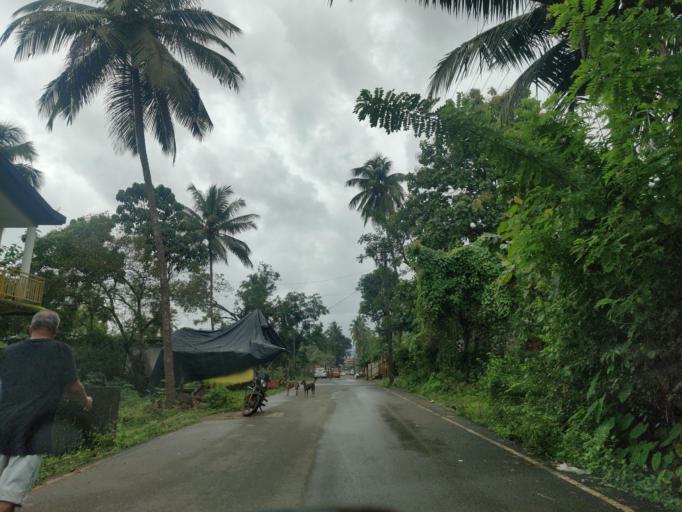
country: IN
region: Goa
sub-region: North Goa
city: Valpoy
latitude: 15.5283
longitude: 74.1379
